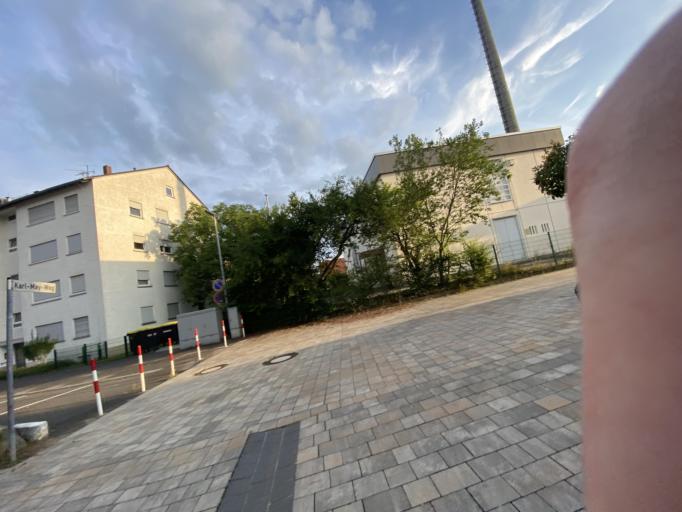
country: DE
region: Hesse
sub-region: Regierungsbezirk Darmstadt
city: Dietzenbach
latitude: 49.9782
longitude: 8.7951
